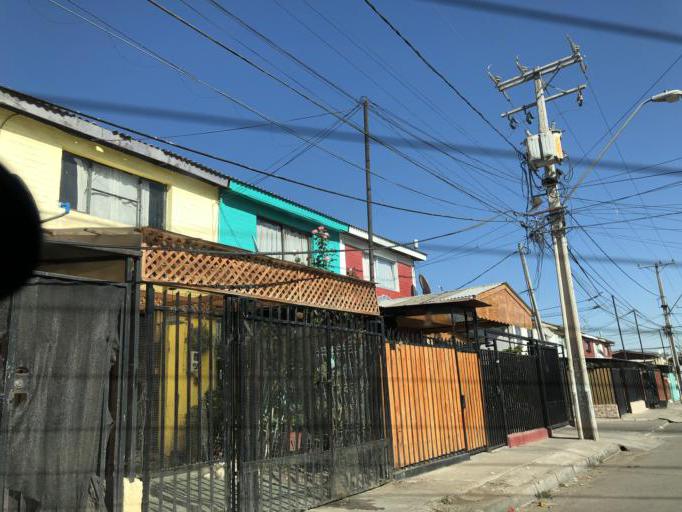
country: CL
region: Santiago Metropolitan
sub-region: Provincia de Santiago
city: La Pintana
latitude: -33.6142
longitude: -70.6183
